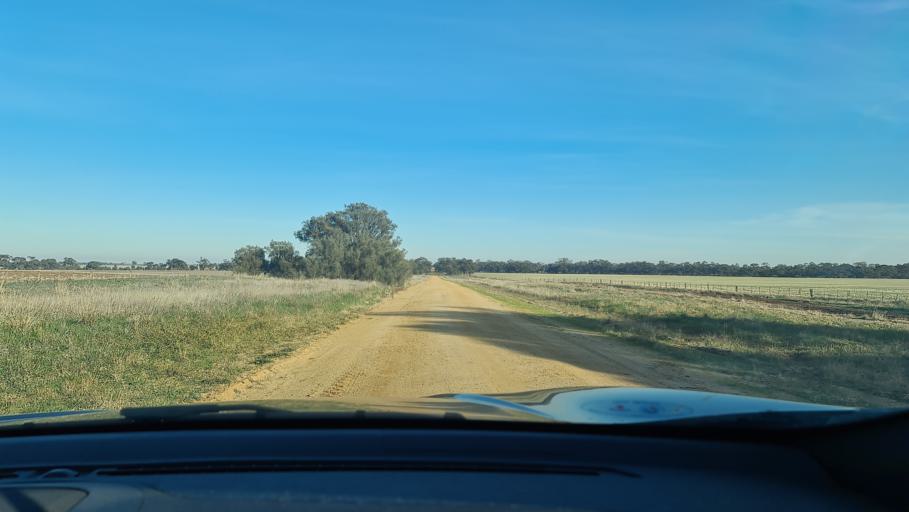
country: AU
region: Victoria
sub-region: Horsham
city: Horsham
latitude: -36.3538
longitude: 142.4058
